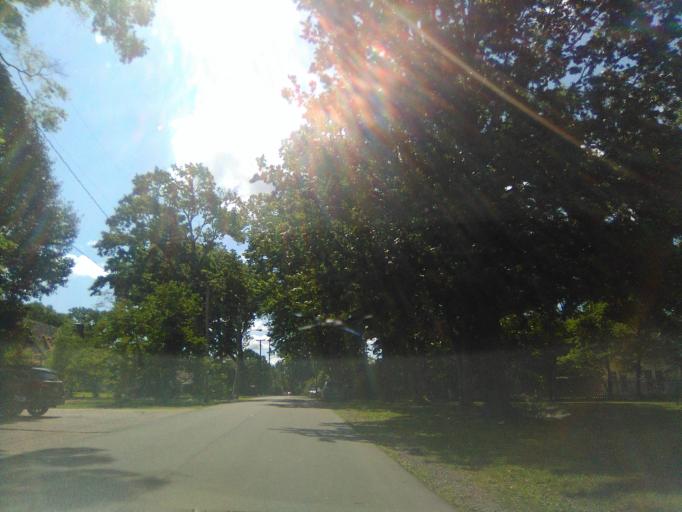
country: US
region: Tennessee
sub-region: Davidson County
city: Belle Meade
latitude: 36.1016
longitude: -86.8652
